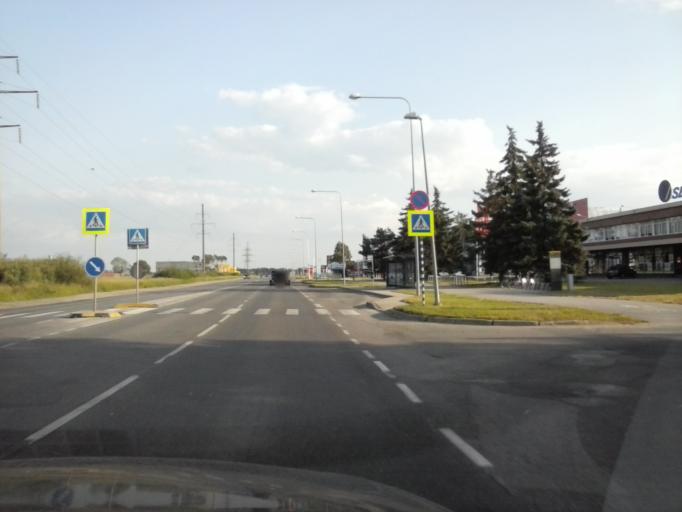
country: EE
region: Tartu
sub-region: Tartu linn
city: Tartu
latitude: 58.3499
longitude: 26.7410
